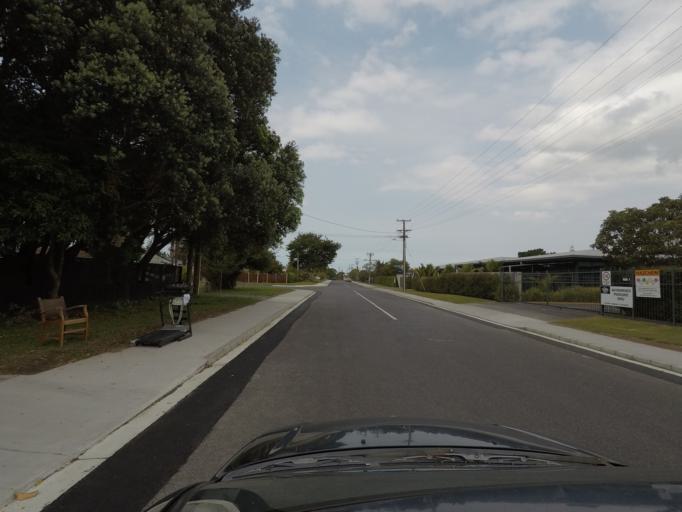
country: NZ
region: Auckland
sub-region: Auckland
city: Rosebank
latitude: -36.8288
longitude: 174.6486
